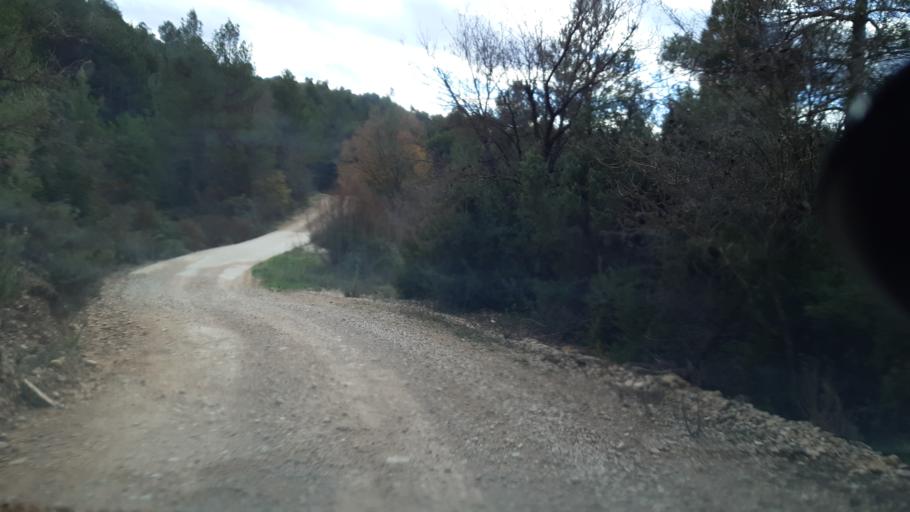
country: ES
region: Aragon
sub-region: Provincia de Teruel
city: Valderrobres
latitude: 40.8520
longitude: 0.2197
